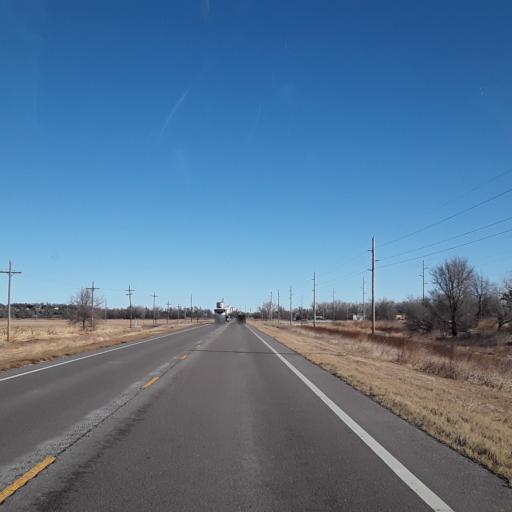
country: US
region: Kansas
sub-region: Pawnee County
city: Larned
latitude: 38.1627
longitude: -99.1175
